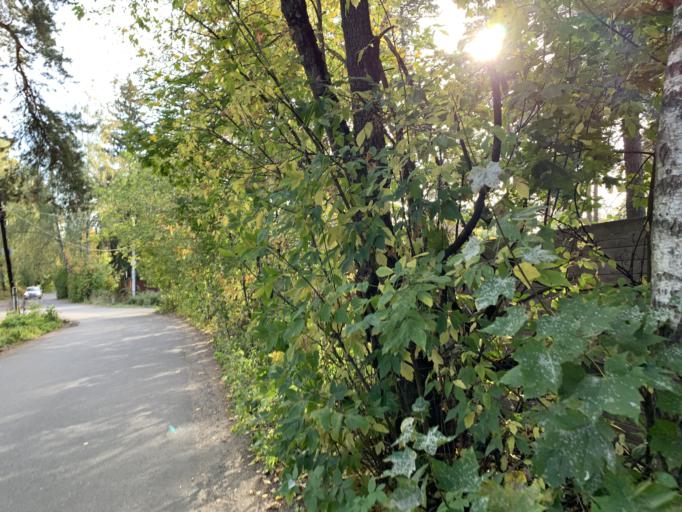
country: RU
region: Moskovskaya
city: Mamontovka
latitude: 55.9863
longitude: 37.8313
